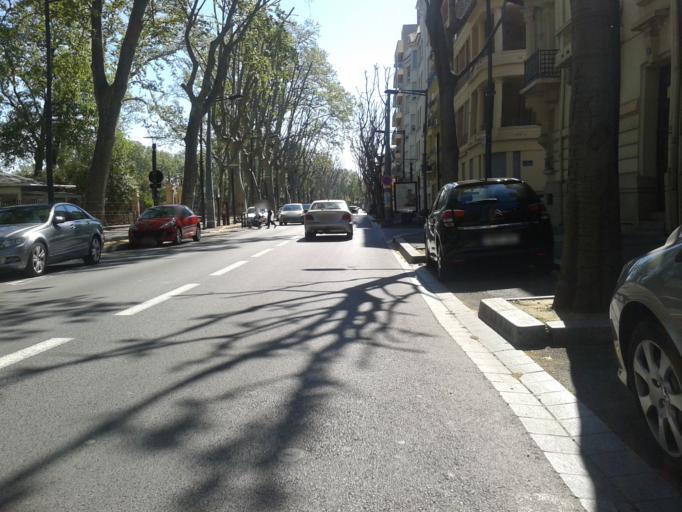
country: FR
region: Languedoc-Roussillon
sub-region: Departement des Pyrenees-Orientales
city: Perpignan
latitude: 42.7018
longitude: 2.8993
